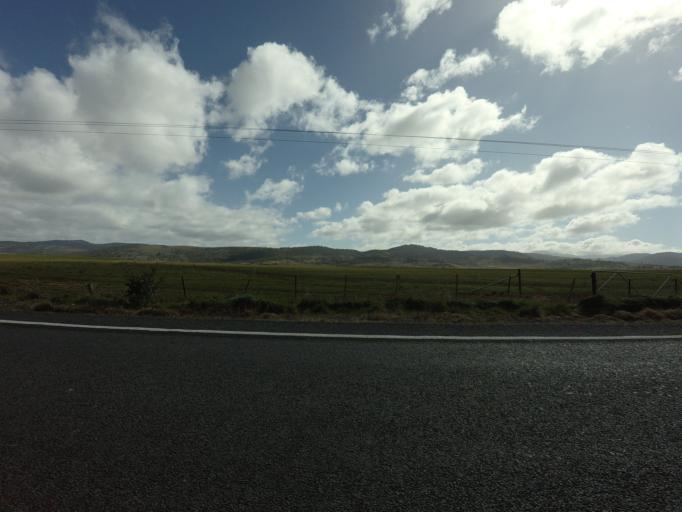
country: AU
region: Tasmania
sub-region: Northern Midlands
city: Evandale
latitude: -41.8034
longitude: 147.6848
